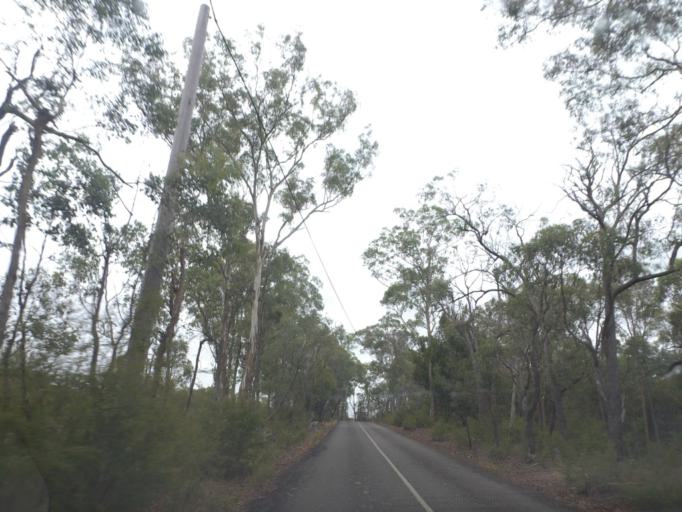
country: AU
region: Victoria
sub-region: Nillumbik
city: North Warrandyte
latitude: -37.7015
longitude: 145.2674
